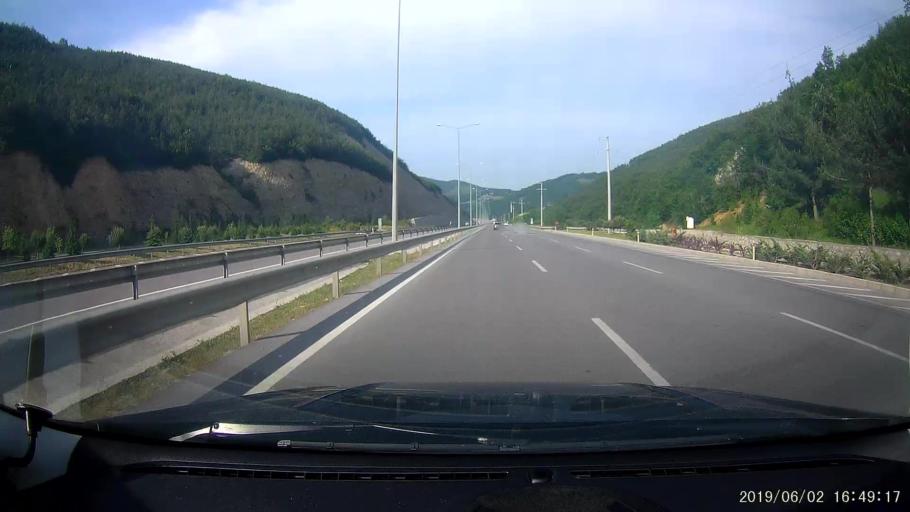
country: TR
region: Samsun
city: Taflan
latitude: 41.2353
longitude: 36.1583
